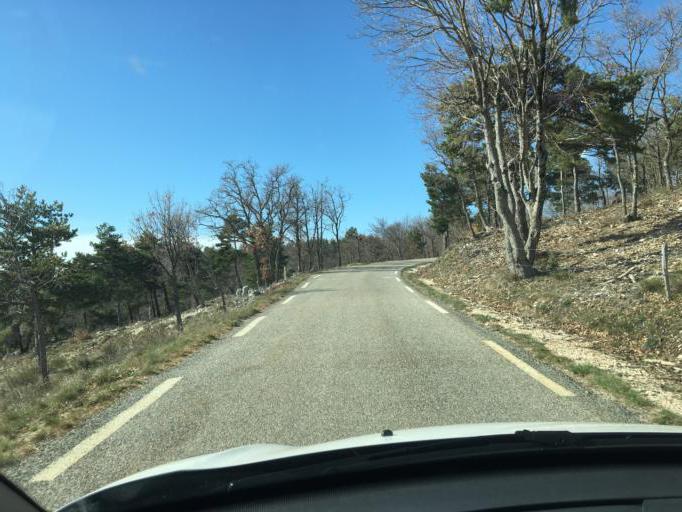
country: FR
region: Provence-Alpes-Cote d'Azur
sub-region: Departement du Vaucluse
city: Saint-Saturnin-les-Apt
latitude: 43.9696
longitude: 5.4623
